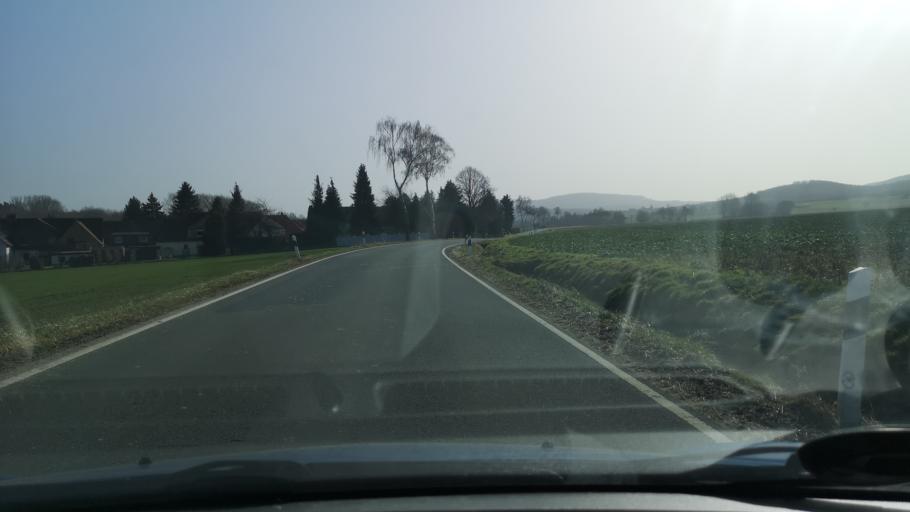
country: DE
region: Lower Saxony
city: Weenzen
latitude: 52.0138
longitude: 9.6291
